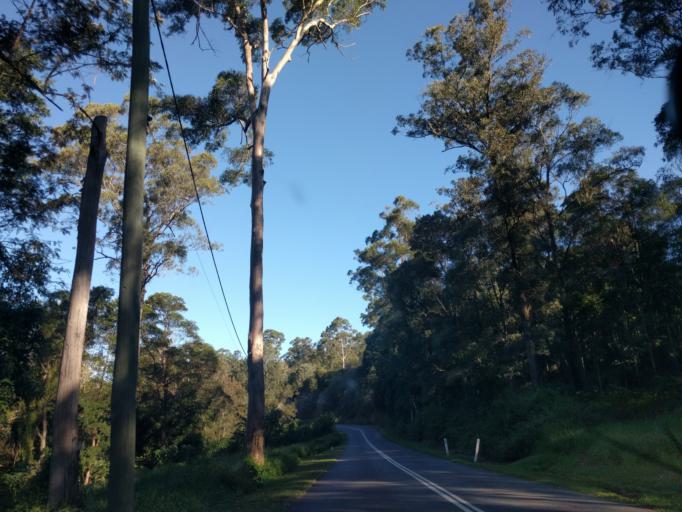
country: AU
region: Queensland
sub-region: Brisbane
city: Pullenvale
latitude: -27.4828
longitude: 152.8770
